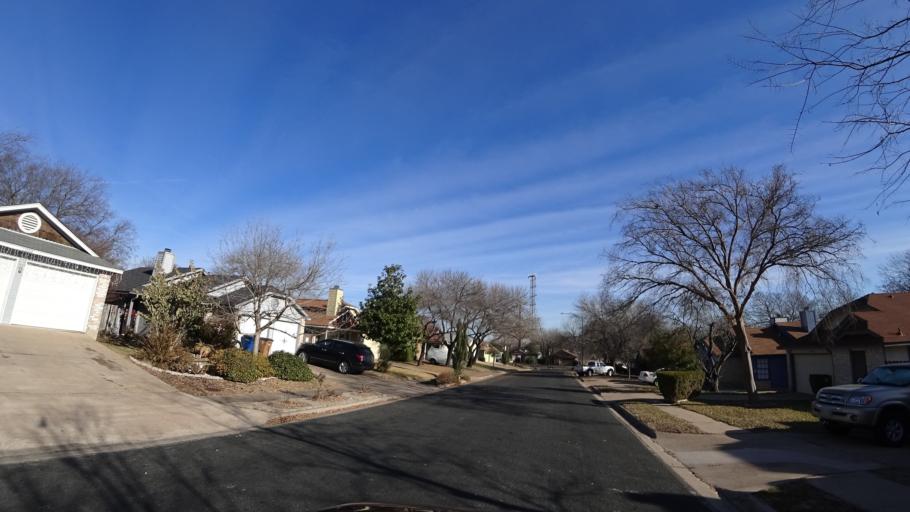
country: US
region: Texas
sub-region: Travis County
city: Wells Branch
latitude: 30.3936
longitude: -97.7042
